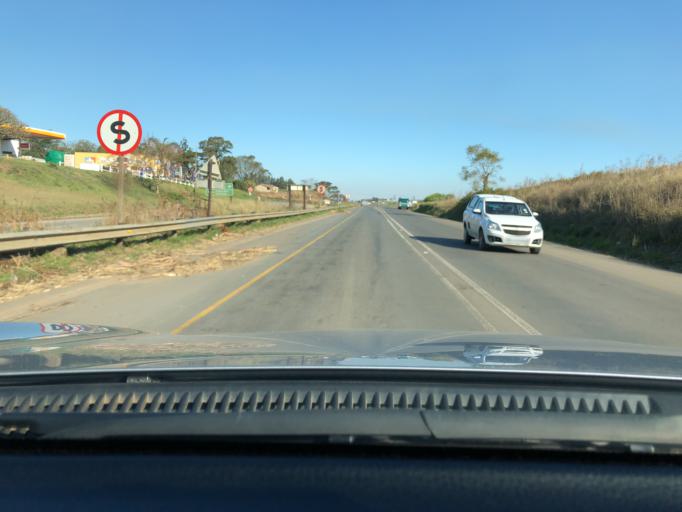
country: ZA
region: KwaZulu-Natal
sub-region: uMgungundlovu District Municipality
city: Camperdown
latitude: -29.7226
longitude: 30.4985
